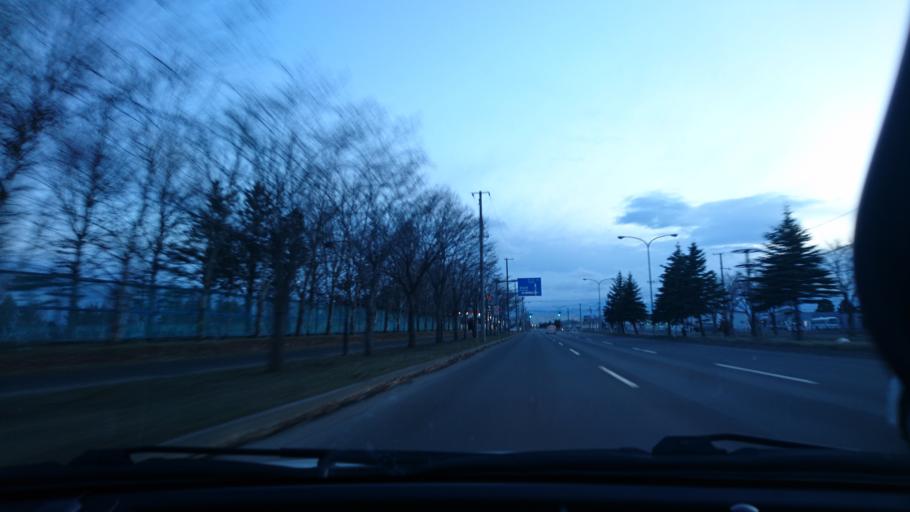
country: JP
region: Hokkaido
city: Sapporo
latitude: 43.1183
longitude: 141.4084
